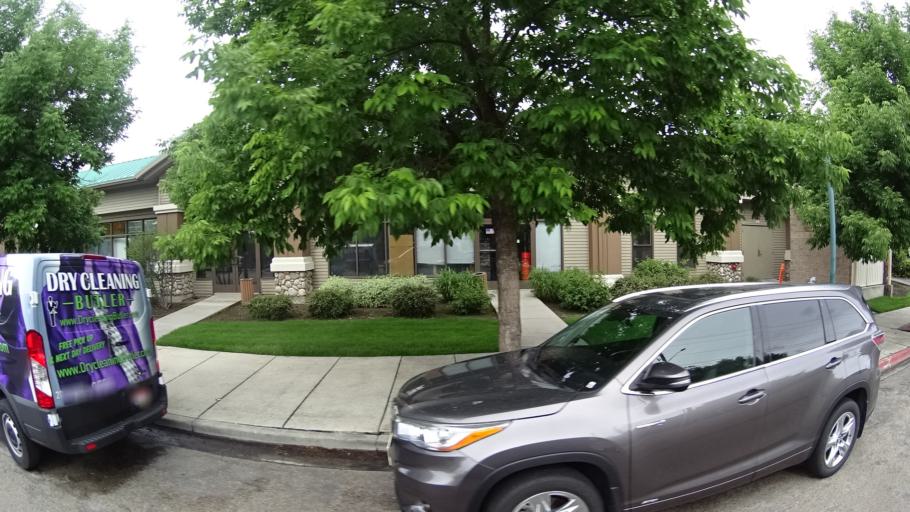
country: US
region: Idaho
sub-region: Ada County
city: Eagle
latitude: 43.6937
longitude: -116.3514
